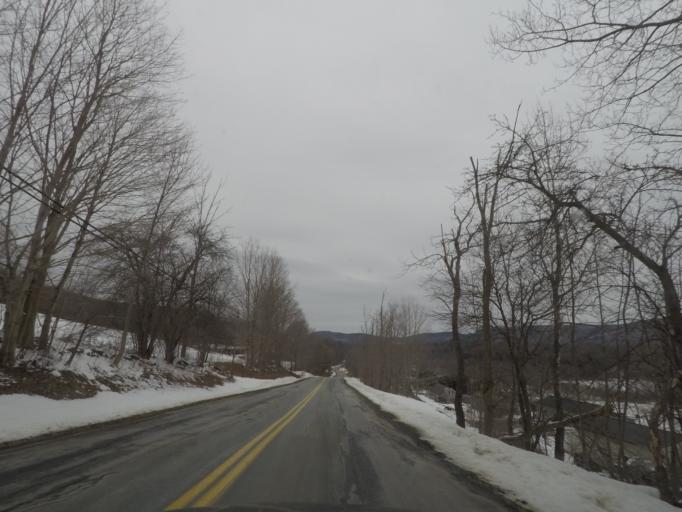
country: US
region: Massachusetts
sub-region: Berkshire County
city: Lanesborough
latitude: 42.5775
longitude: -73.3766
